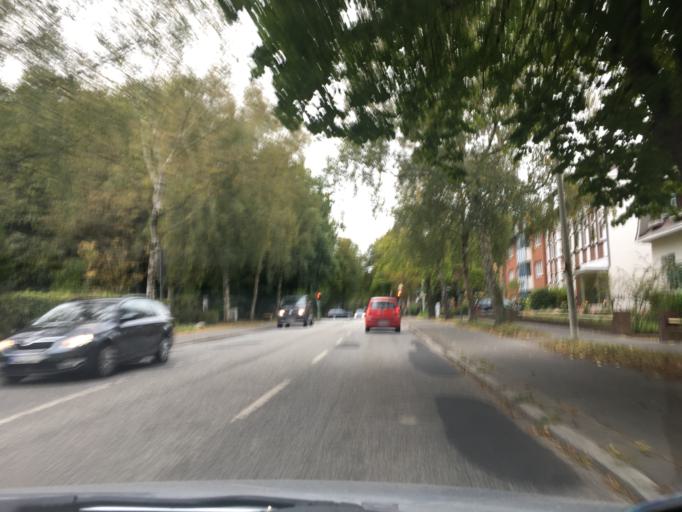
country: DE
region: Schleswig-Holstein
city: Kronshagen
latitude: 54.3198
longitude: 10.0889
